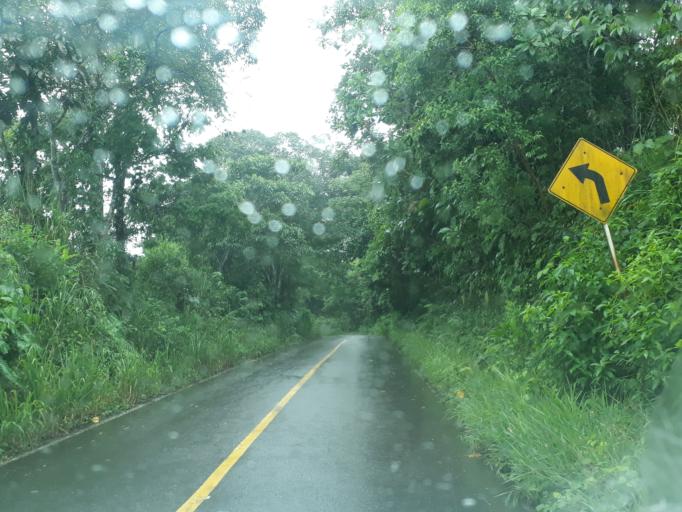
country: CO
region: Cundinamarca
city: Paratebueno
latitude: 4.4006
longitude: -73.3042
